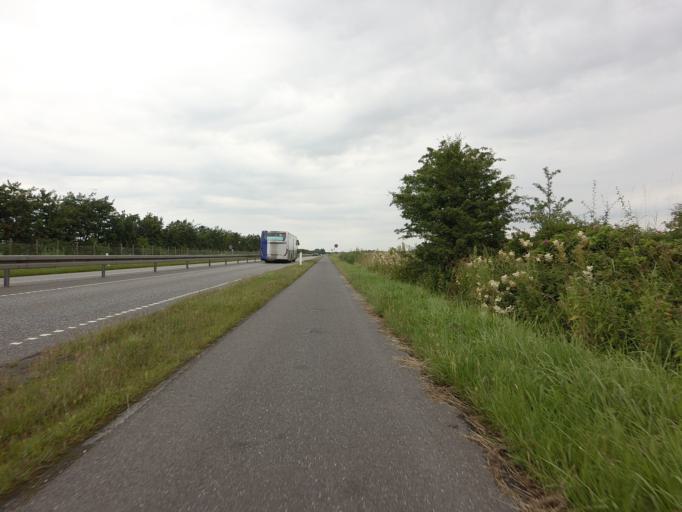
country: DK
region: North Denmark
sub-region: Alborg Kommune
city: Vadum
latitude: 57.0919
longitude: 9.8873
